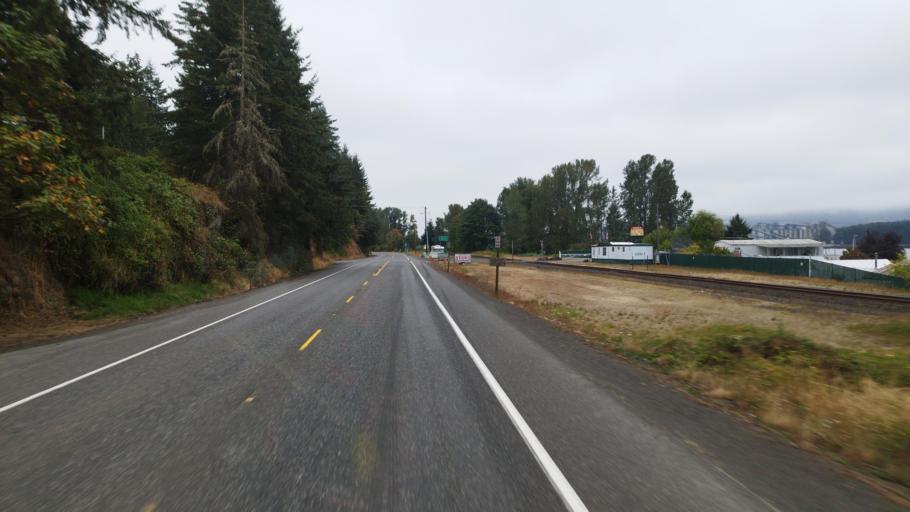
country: US
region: Washington
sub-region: Cowlitz County
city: Kalama
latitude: 46.0149
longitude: -122.8752
